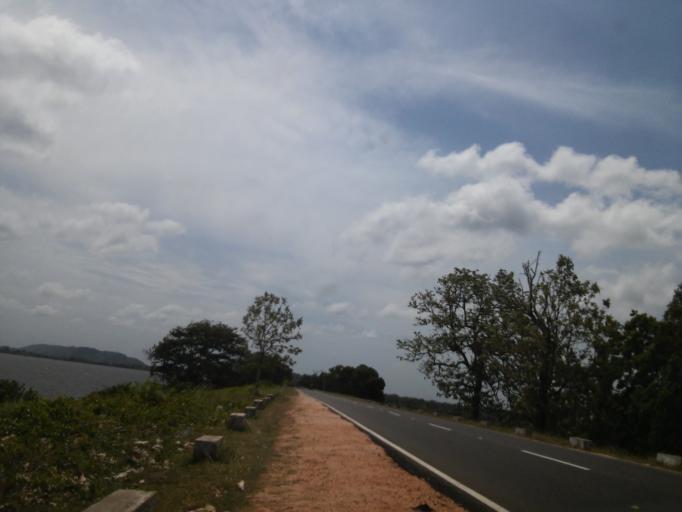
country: LK
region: Eastern Province
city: Trincomalee
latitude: 8.3569
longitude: 80.9854
